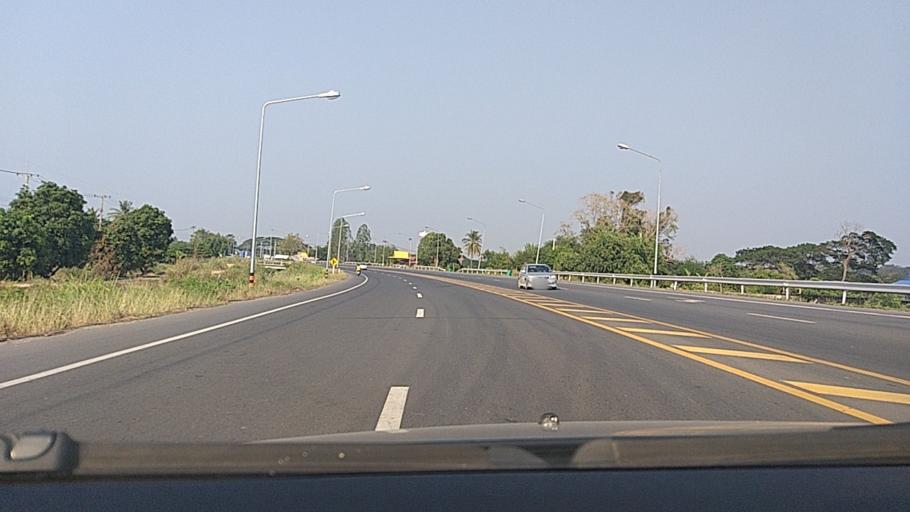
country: TH
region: Sing Buri
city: Phrom Buri
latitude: 14.7899
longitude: 100.4428
